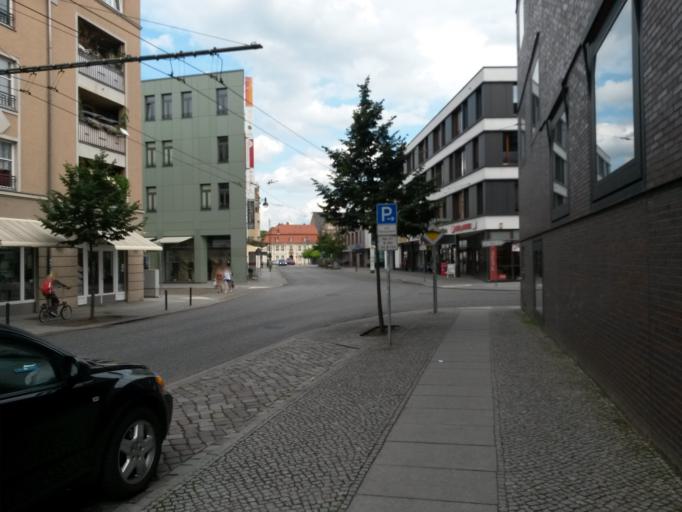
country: DE
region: Brandenburg
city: Eberswalde
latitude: 52.8334
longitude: 13.8182
